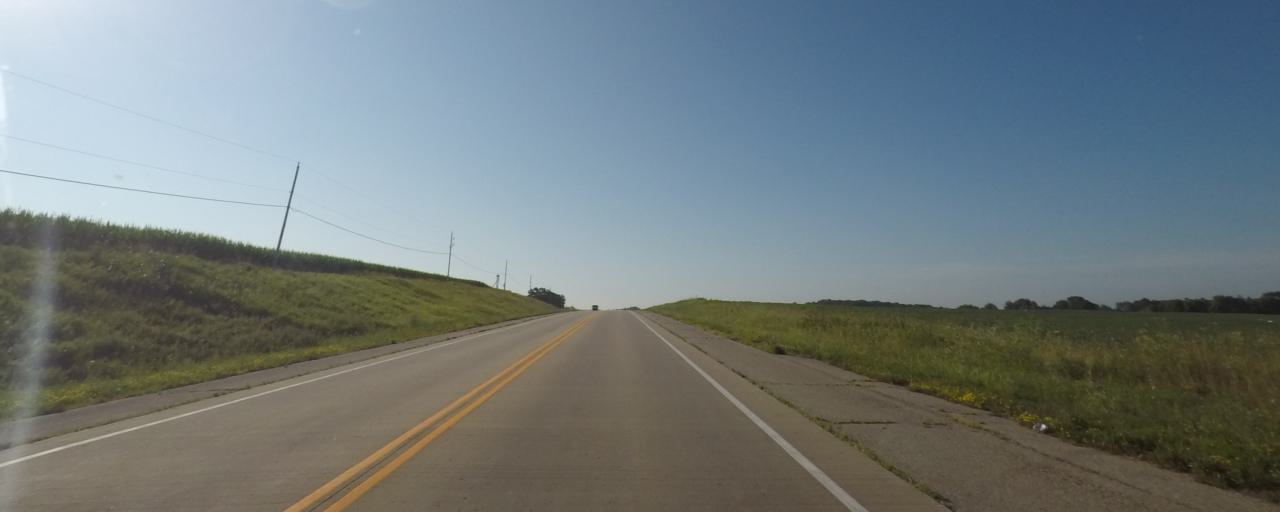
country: US
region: Wisconsin
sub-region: Jefferson County
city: Lake Ripley
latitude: 42.9846
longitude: -88.9709
